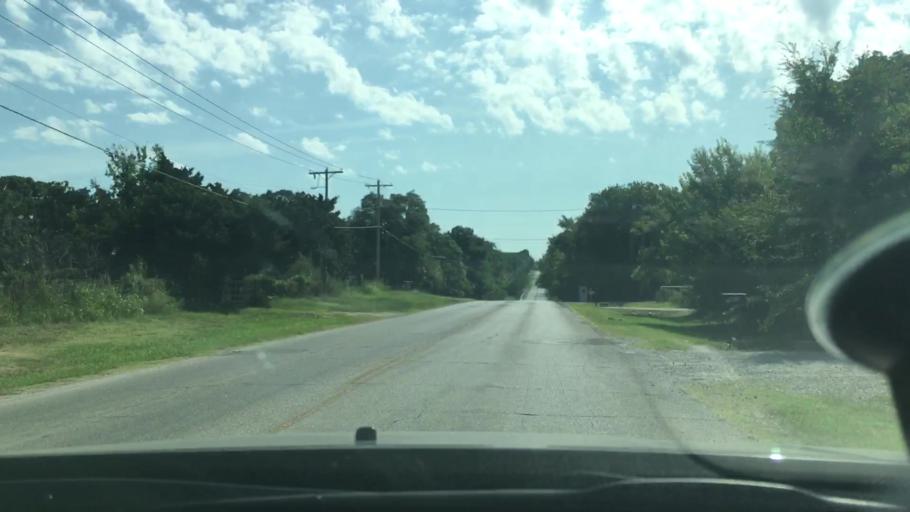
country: US
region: Oklahoma
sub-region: Carter County
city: Ardmore
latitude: 34.1583
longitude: -97.0989
